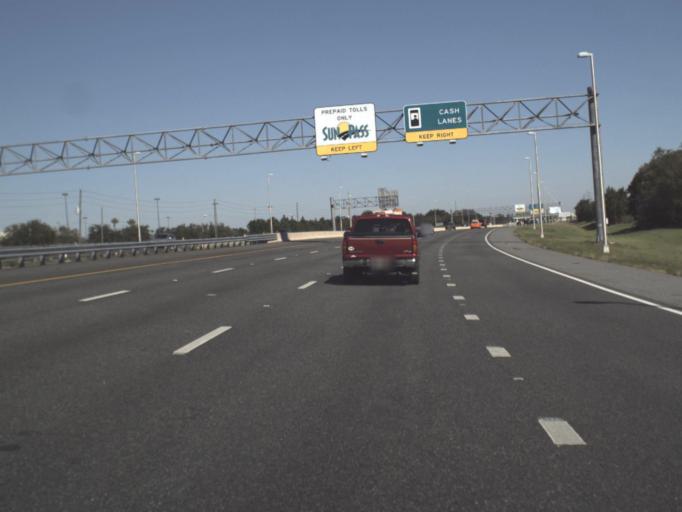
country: US
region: Florida
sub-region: Orange County
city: Sky Lake
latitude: 28.4411
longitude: -81.3948
